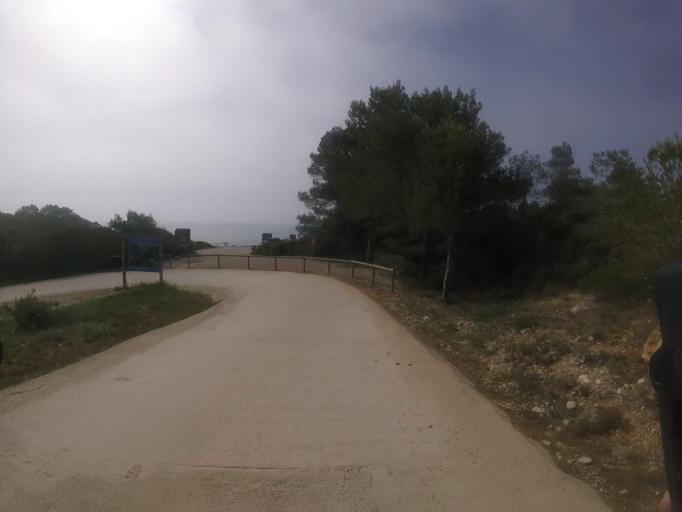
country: ES
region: Valencia
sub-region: Provincia de Castello
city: Alcoceber
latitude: 40.2791
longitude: 0.3268
